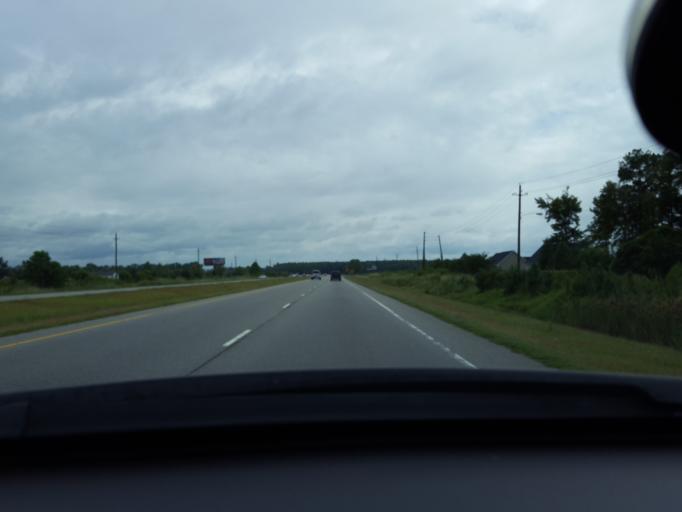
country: US
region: North Carolina
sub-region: Pitt County
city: Ayden
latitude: 35.4708
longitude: -77.4358
